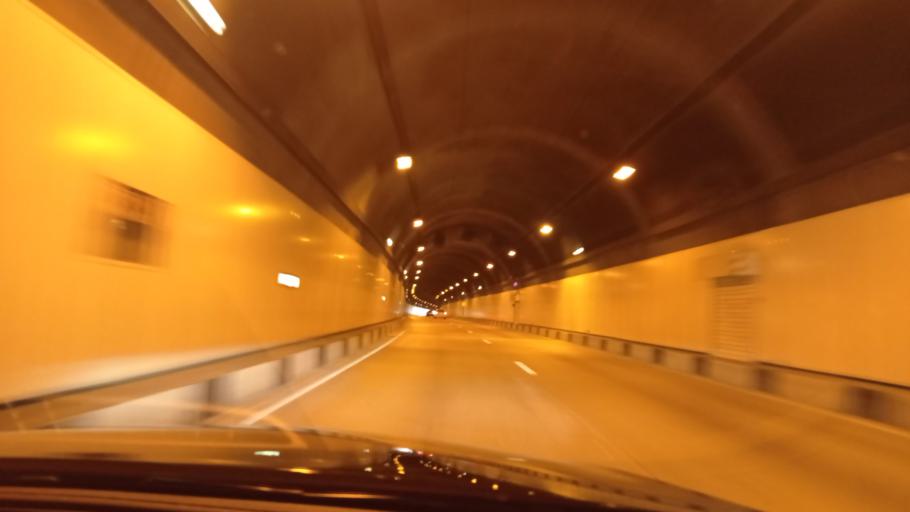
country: RU
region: Krasnodarskiy
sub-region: Sochi City
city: Khosta
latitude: 43.5202
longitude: 39.8490
